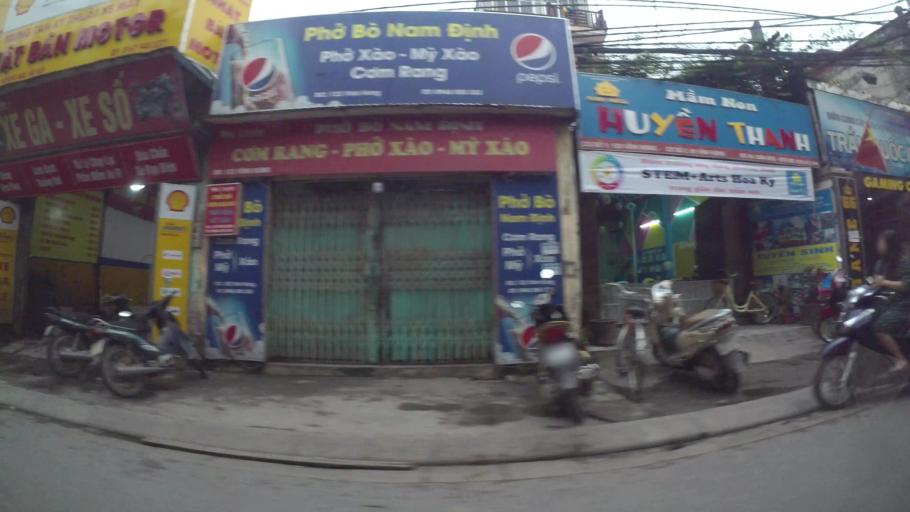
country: VN
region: Ha Noi
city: Hai BaTrung
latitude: 20.9879
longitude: 105.8771
